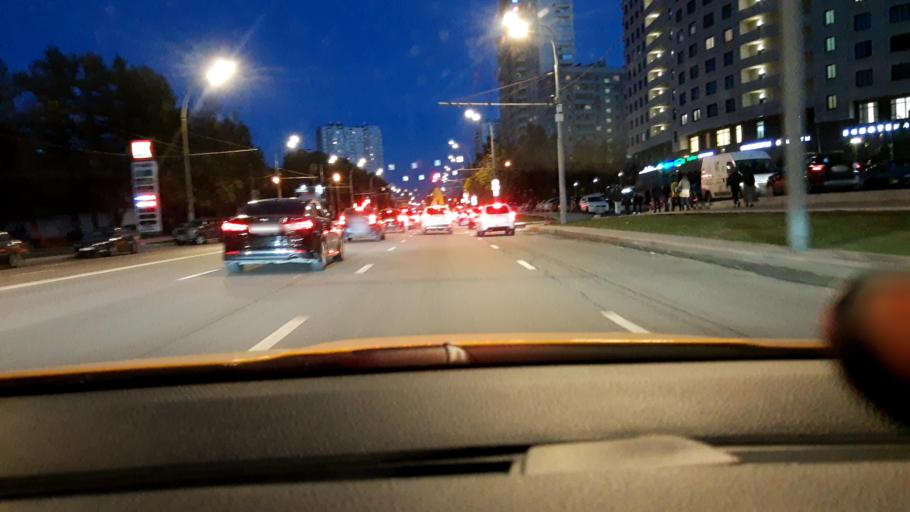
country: RU
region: Moskovskaya
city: Cheremushki
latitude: 55.6594
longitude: 37.5602
